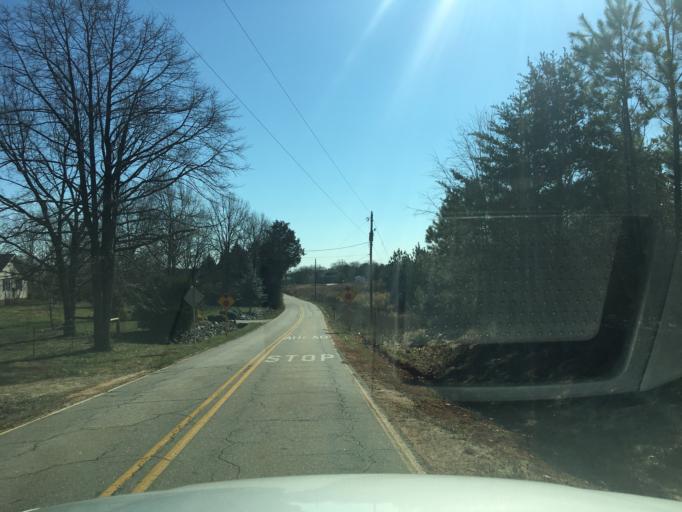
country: US
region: South Carolina
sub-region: Pickens County
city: Pickens
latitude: 34.8275
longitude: -82.7845
